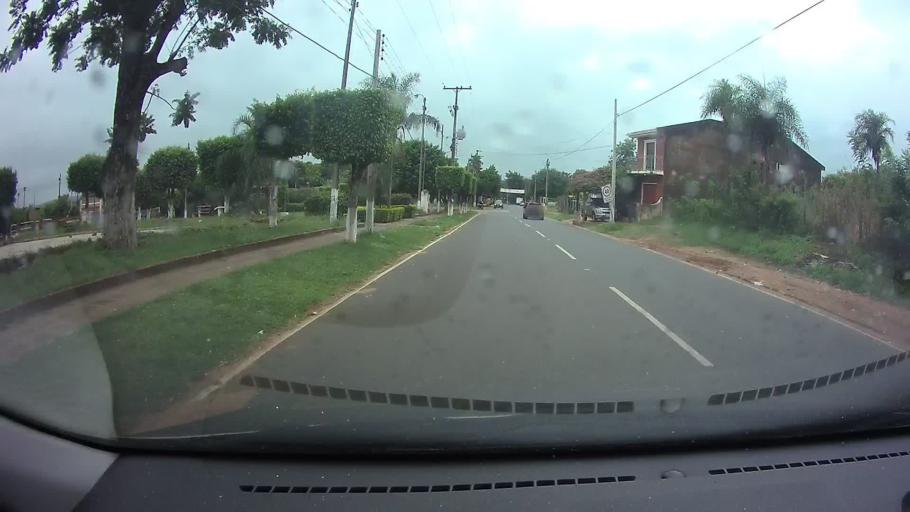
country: PY
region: Paraguari
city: Carapegua
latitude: -25.7634
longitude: -57.2503
